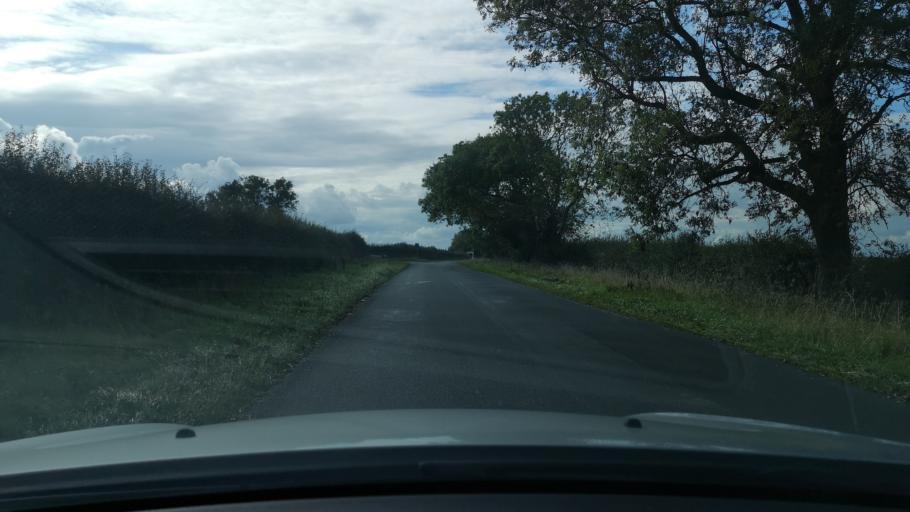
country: GB
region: England
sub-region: East Riding of Yorkshire
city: Walkington
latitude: 53.8256
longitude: -0.5242
